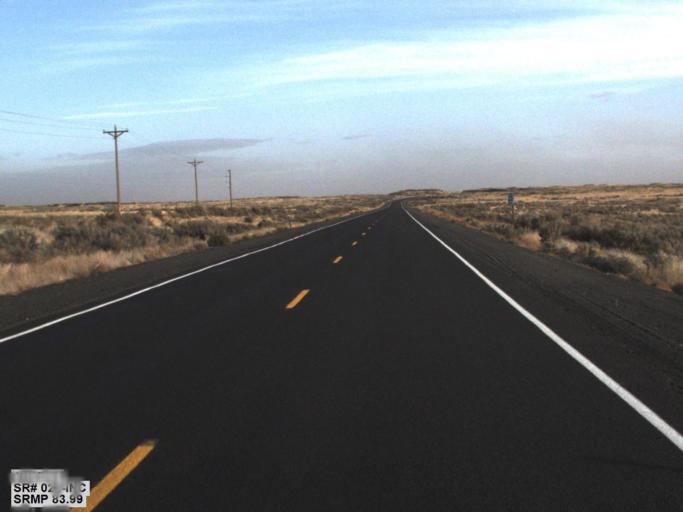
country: US
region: Washington
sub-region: Grant County
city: Warden
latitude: 47.3327
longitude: -118.8856
